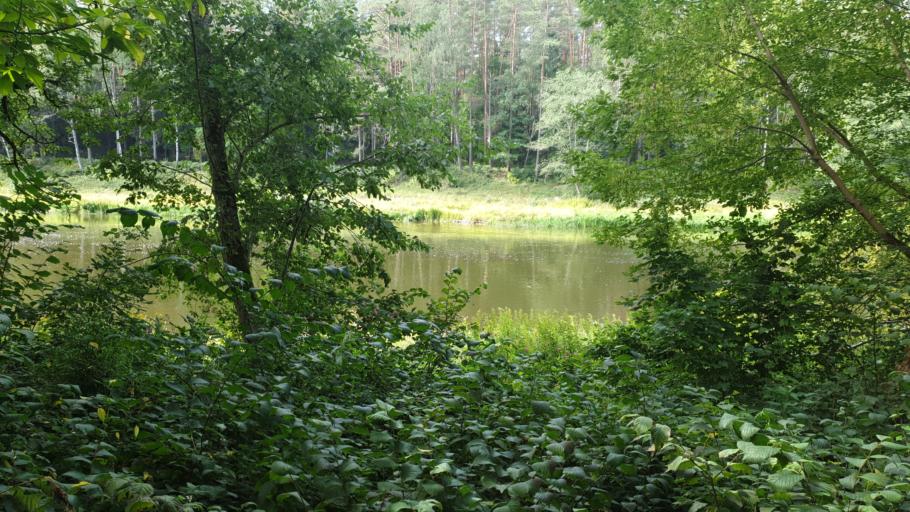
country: LT
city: Grigiskes
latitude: 54.8036
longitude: 24.9749
